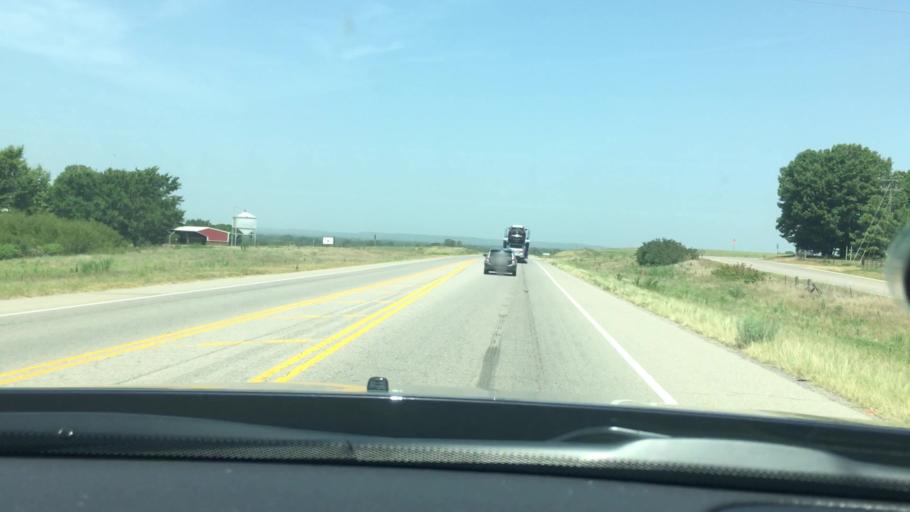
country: US
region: Oklahoma
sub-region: Pontotoc County
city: Ada
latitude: 34.6797
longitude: -96.5813
